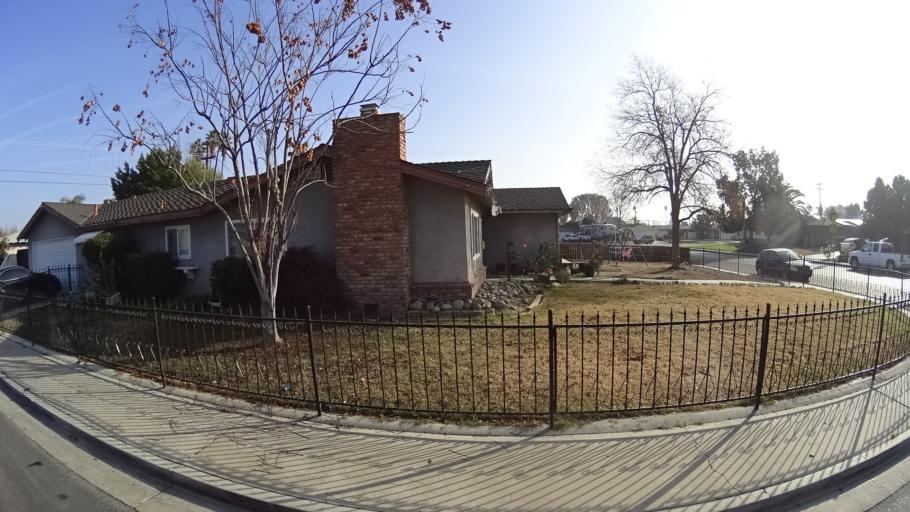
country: US
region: California
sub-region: Kern County
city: Bakersfield
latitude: 35.3283
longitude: -119.0270
